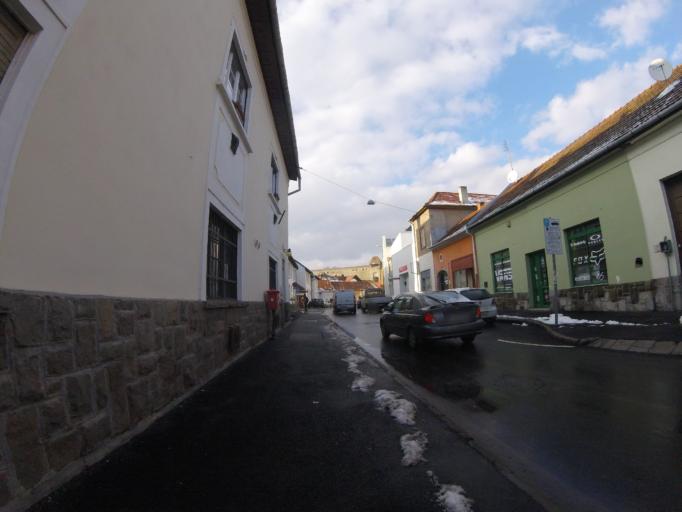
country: HU
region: Heves
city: Eger
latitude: 47.9016
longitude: 20.3815
